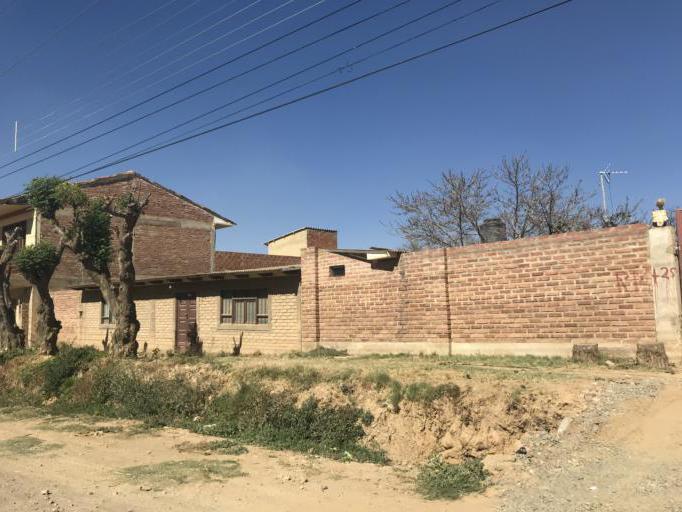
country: BO
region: Cochabamba
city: Cliza
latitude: -17.5748
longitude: -65.9029
